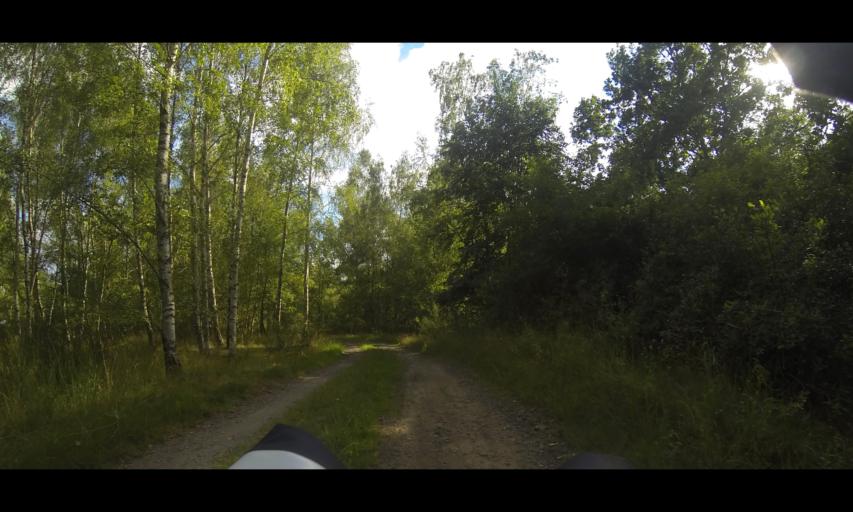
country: DE
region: Saxony
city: Konigsbruck
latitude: 51.2888
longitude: 13.8842
